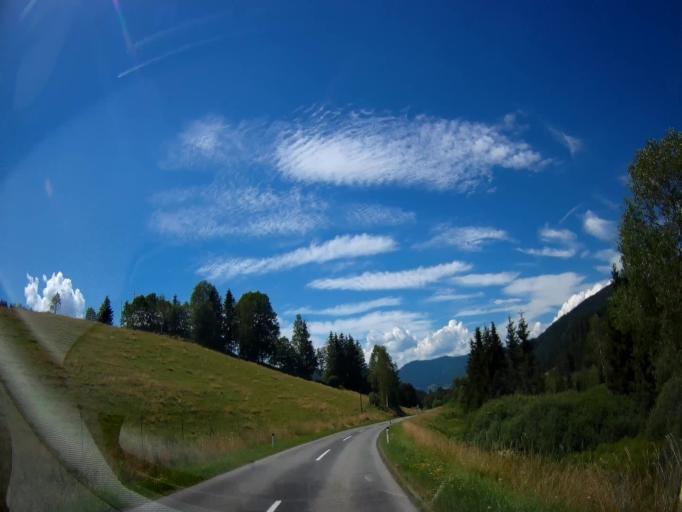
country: AT
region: Carinthia
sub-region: Politischer Bezirk Sankt Veit an der Glan
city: Glodnitz
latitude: 46.8563
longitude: 14.1334
